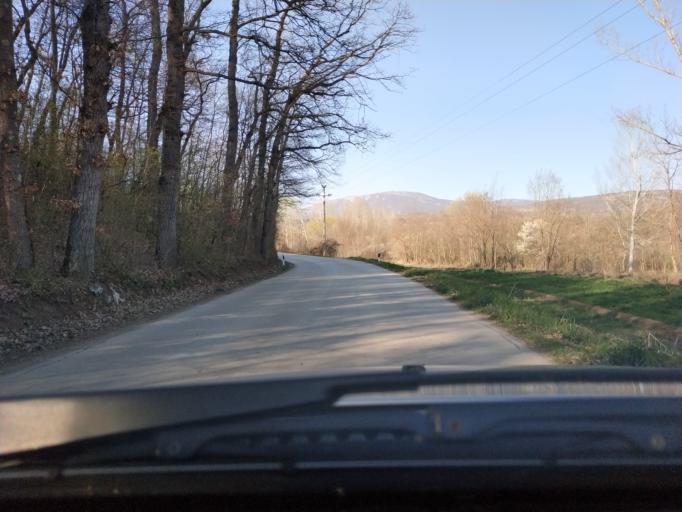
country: RS
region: Central Serbia
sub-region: Nisavski Okrug
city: Aleksinac
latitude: 43.5248
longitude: 21.8015
